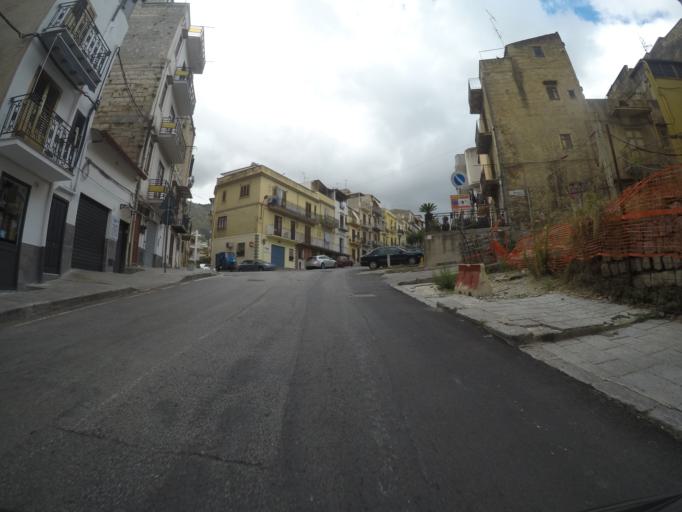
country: IT
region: Sicily
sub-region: Palermo
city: Carini
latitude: 38.1326
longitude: 13.1856
